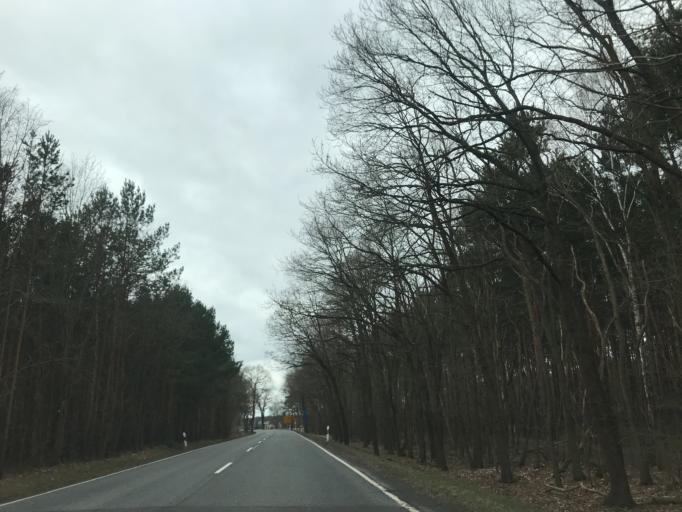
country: DE
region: Brandenburg
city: Golssen
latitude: 51.9765
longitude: 13.6377
